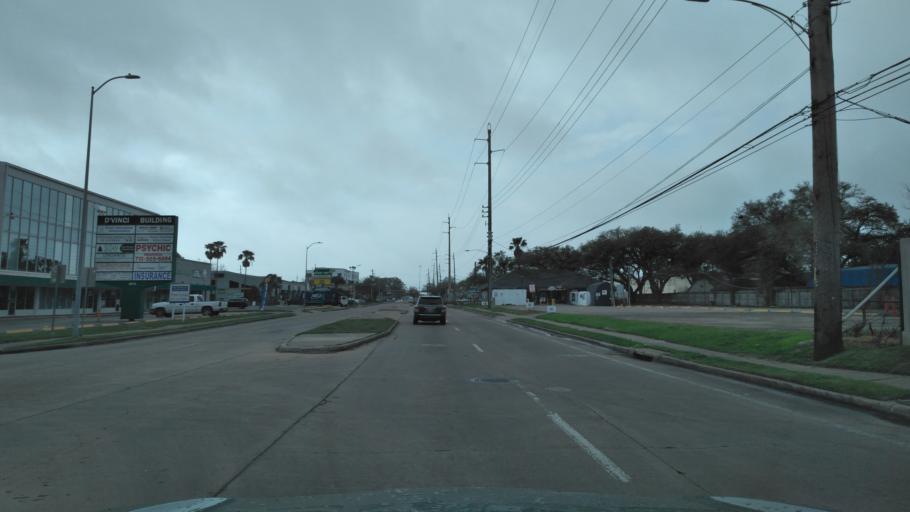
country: US
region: Texas
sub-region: Harris County
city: Hunters Creek Village
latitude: 29.7344
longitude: -95.4842
